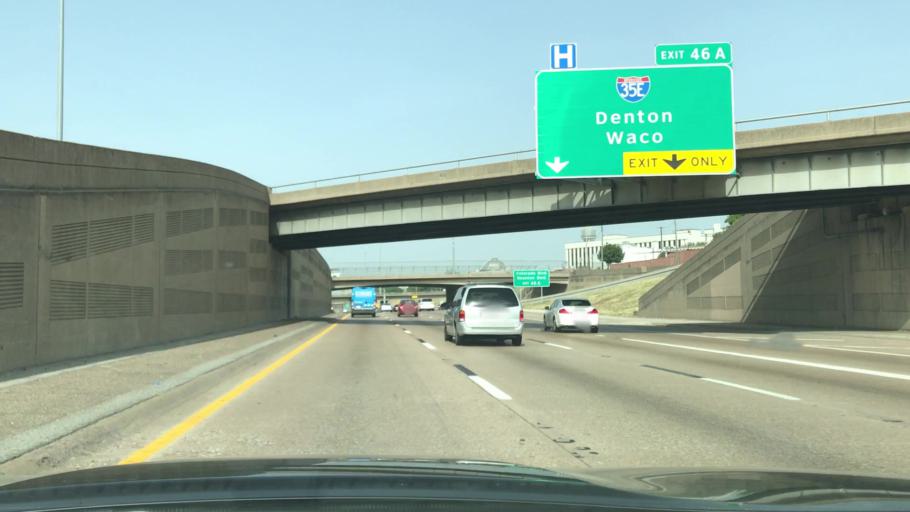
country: US
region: Texas
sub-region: Dallas County
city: Dallas
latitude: 32.7749
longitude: -96.7898
